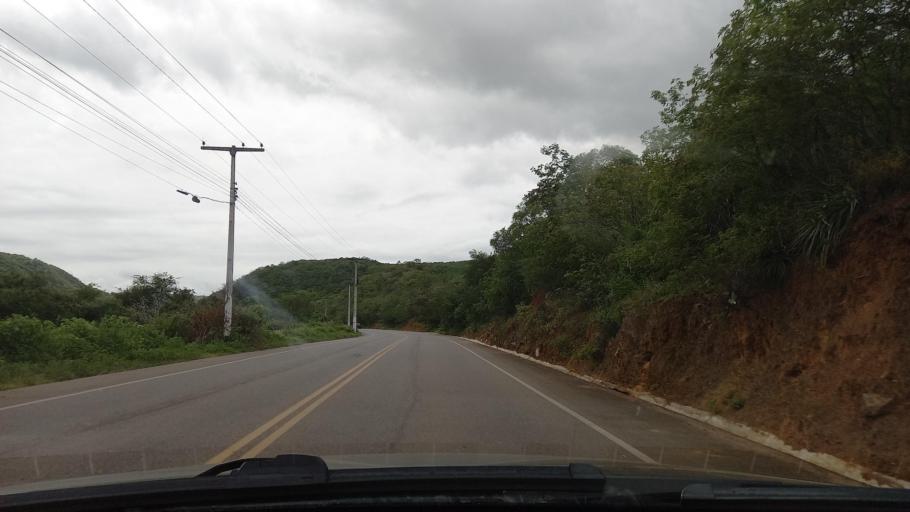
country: BR
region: Sergipe
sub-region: Caninde De Sao Francisco
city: Caninde de Sao Francisco
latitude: -9.6408
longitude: -37.7760
